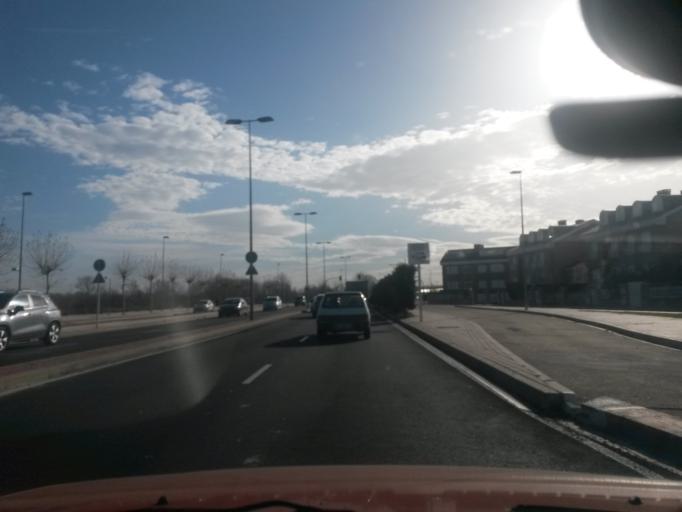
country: ES
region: Castille and Leon
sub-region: Provincia de Salamanca
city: Santa Marta de Tormes
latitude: 40.9571
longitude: -5.6445
